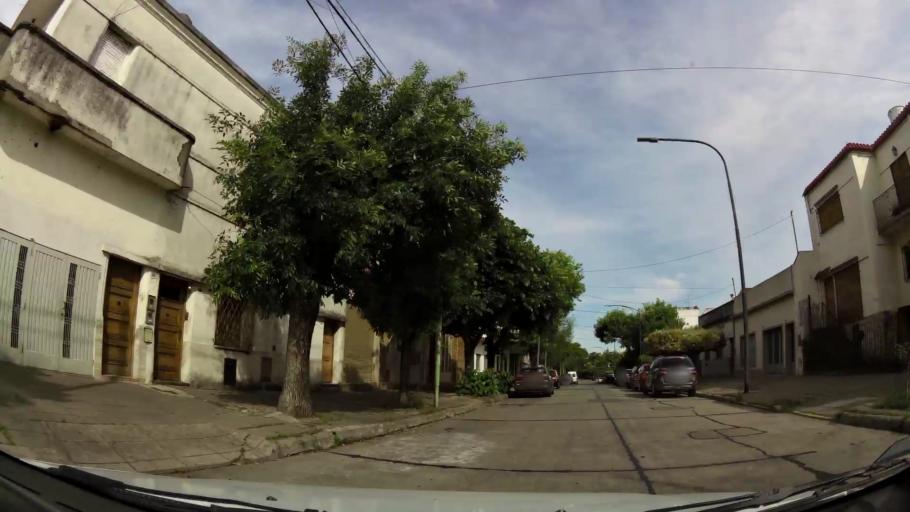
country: AR
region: Buenos Aires F.D.
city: Villa Lugano
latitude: -34.6510
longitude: -58.4804
